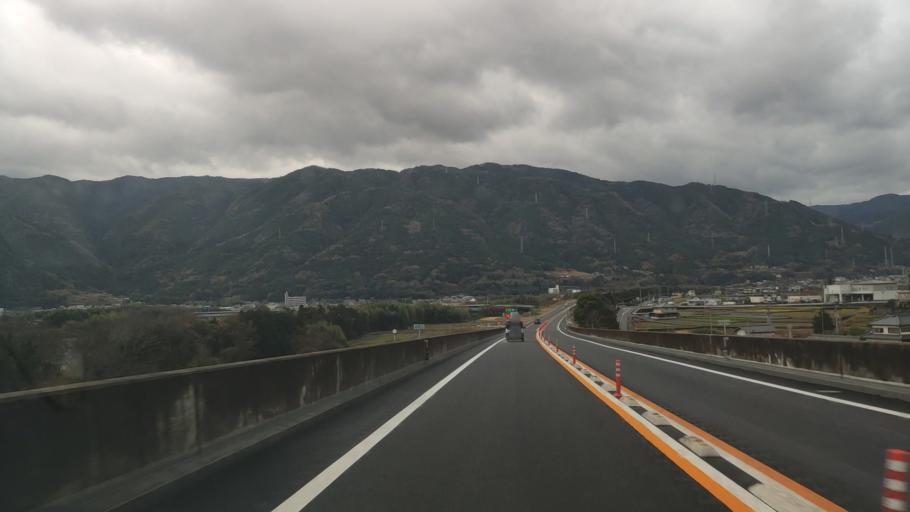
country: JP
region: Tokushima
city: Ikedacho
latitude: 34.0461
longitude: 133.9130
